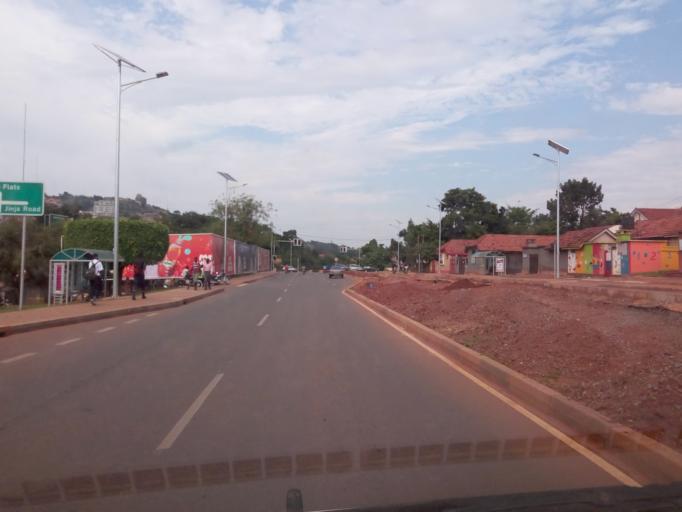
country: UG
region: Central Region
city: Kampala Central Division
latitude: 0.3431
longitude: 32.5942
